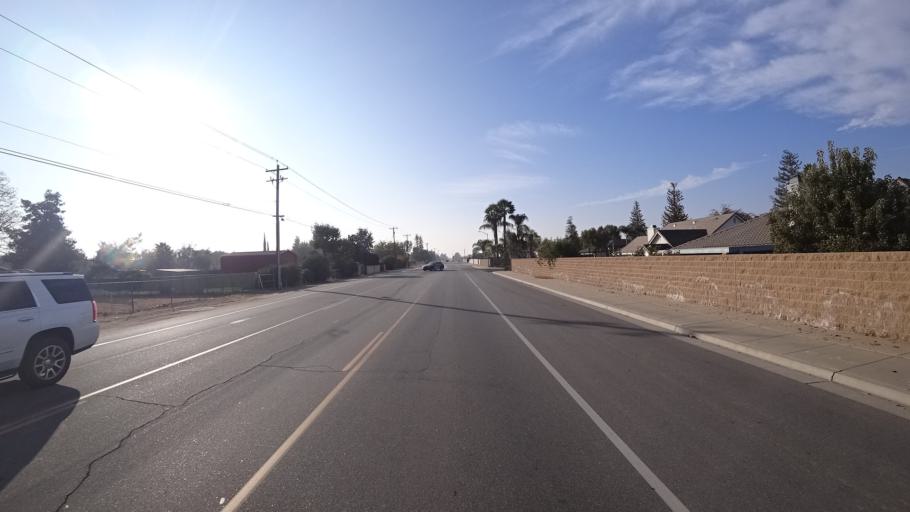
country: US
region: California
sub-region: Kern County
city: Rosedale
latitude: 35.3730
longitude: -119.1634
